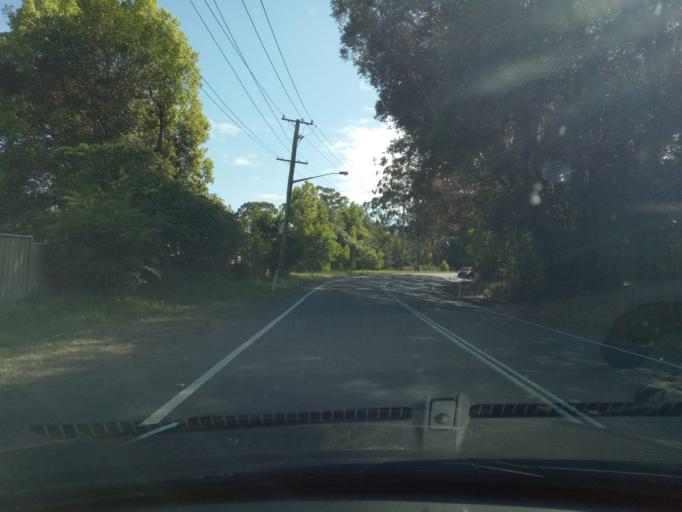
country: AU
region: New South Wales
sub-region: Gosford Shire
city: Narara
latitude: -33.3908
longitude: 151.3536
